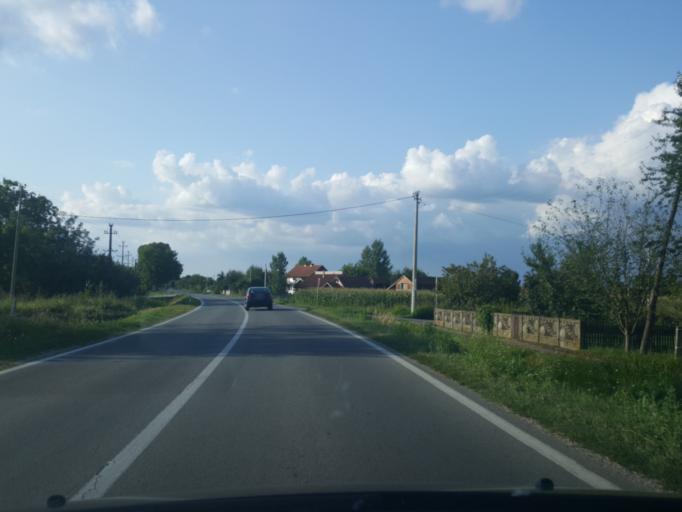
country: RS
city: Lipnicki Sor
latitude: 44.5916
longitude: 19.2584
